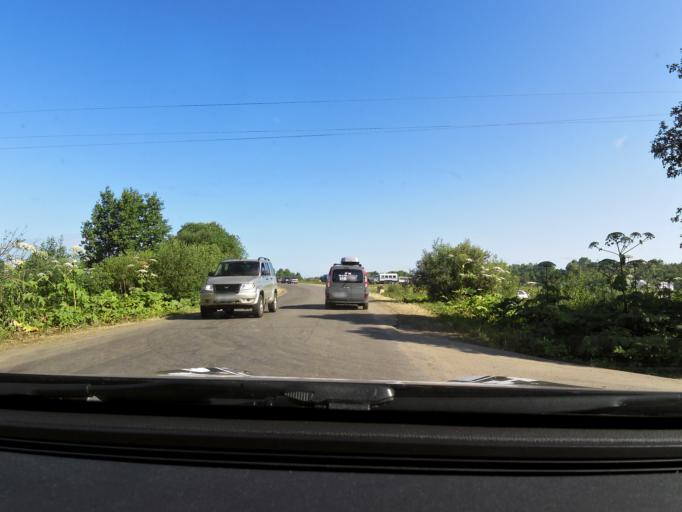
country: RU
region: Tverskaya
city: Zavidovo
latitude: 56.6093
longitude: 36.6369
